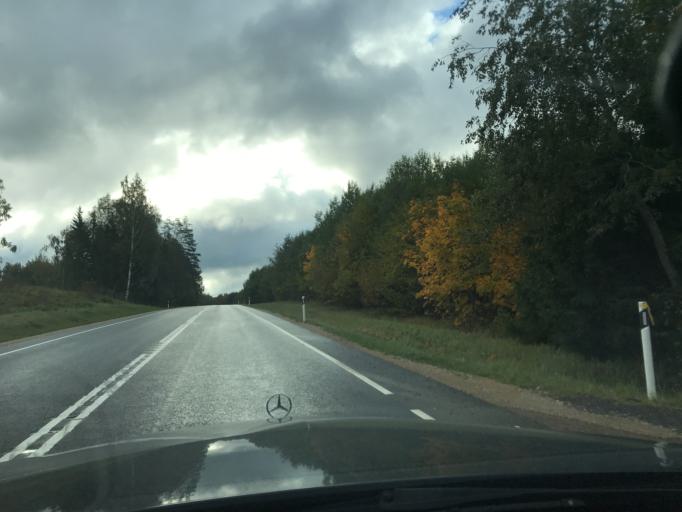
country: EE
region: Viljandimaa
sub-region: Karksi vald
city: Karksi-Nuia
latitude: 58.0586
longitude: 25.6288
